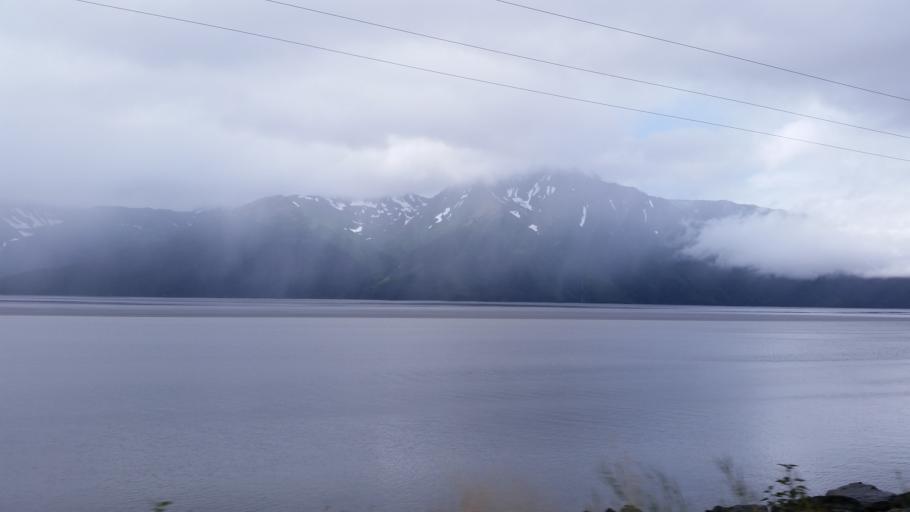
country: US
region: Alaska
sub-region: Anchorage Municipality
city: Girdwood
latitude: 60.9370
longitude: -149.2794
